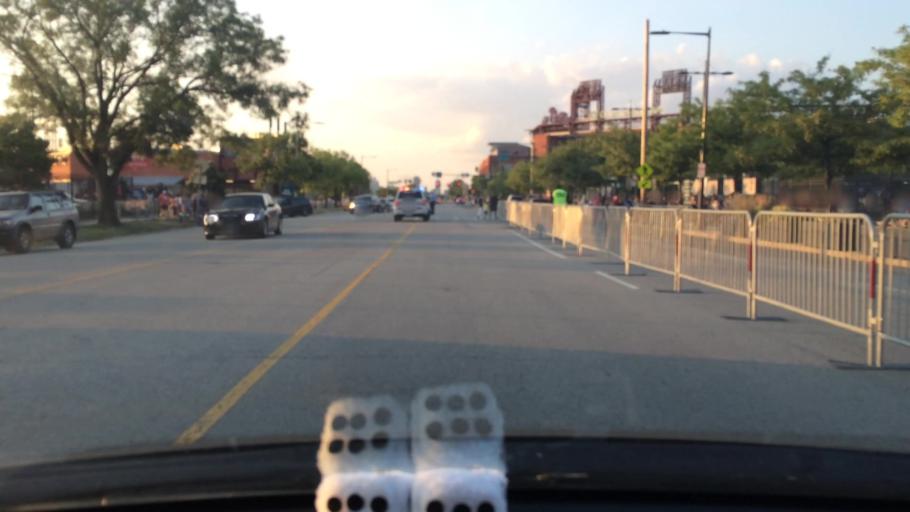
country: US
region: New Jersey
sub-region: Gloucester County
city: National Park
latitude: 39.9026
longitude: -75.1690
